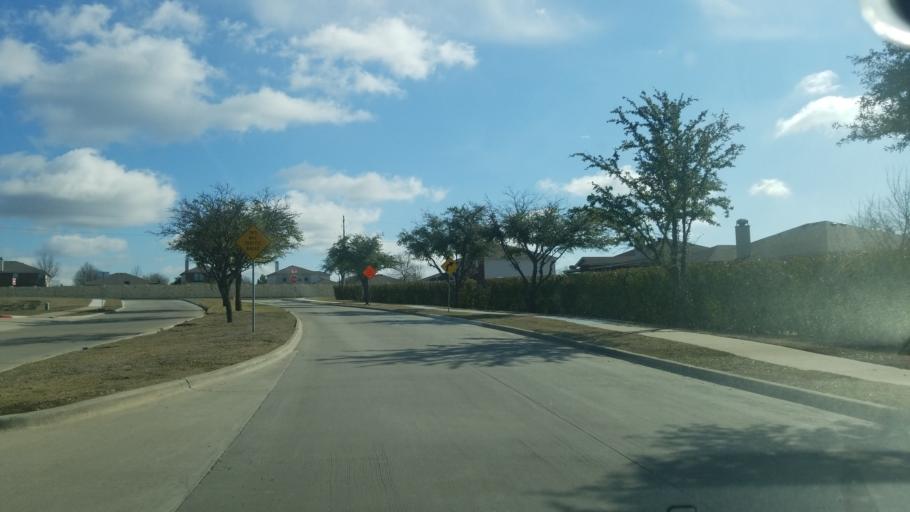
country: US
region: Texas
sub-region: Rockwall County
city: Rockwall
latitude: 32.9053
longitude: -96.4383
